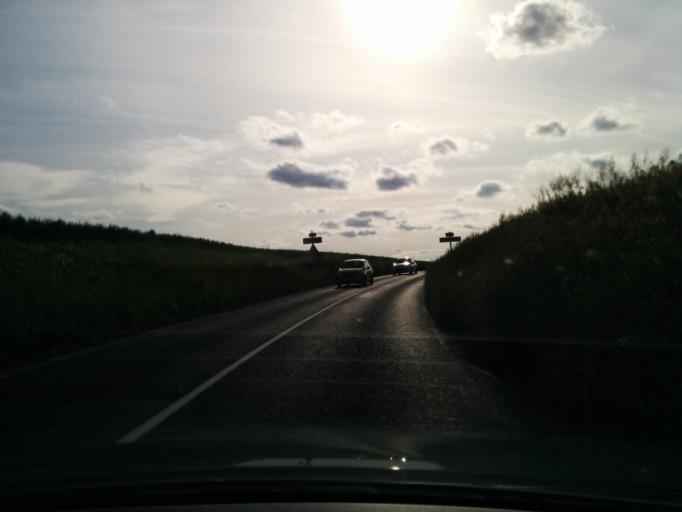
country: FR
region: Haute-Normandie
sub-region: Departement de l'Eure
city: Courcelles-sur-Seine
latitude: 49.1752
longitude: 1.3922
